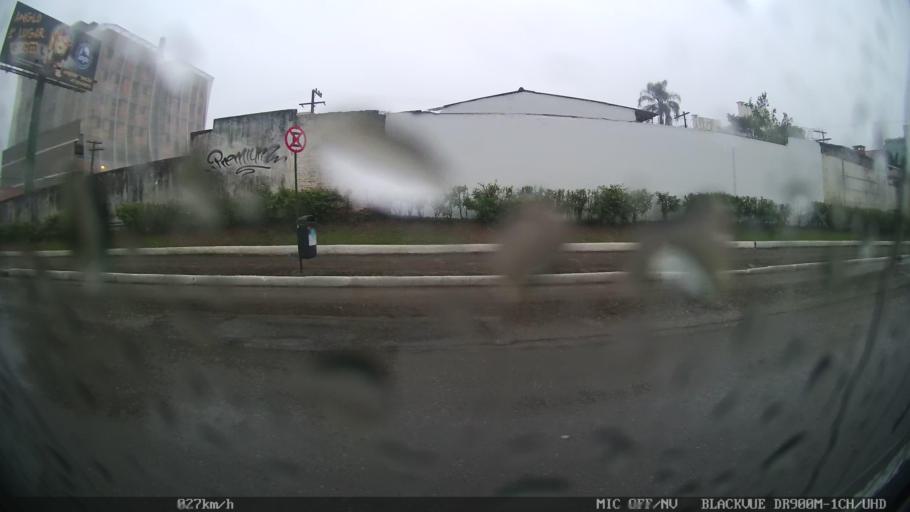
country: BR
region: Santa Catarina
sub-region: Balneario Camboriu
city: Balneario Camboriu
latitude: -26.9764
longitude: -48.6428
